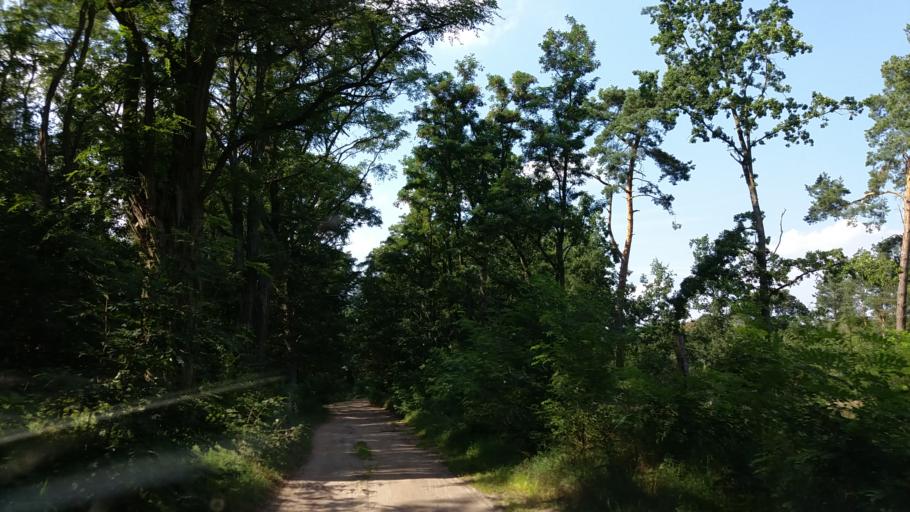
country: PL
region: West Pomeranian Voivodeship
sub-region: Powiat choszczenski
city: Choszczno
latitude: 53.1003
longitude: 15.4198
